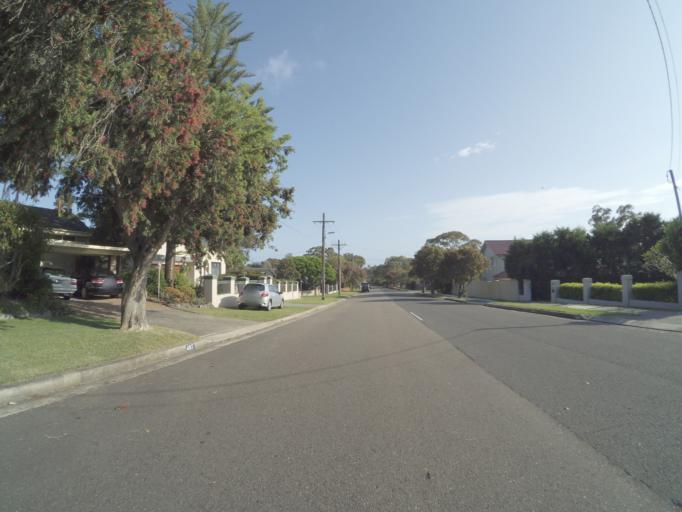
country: AU
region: New South Wales
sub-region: Sutherland Shire
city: Dolans Bay
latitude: -34.0684
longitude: 151.1378
